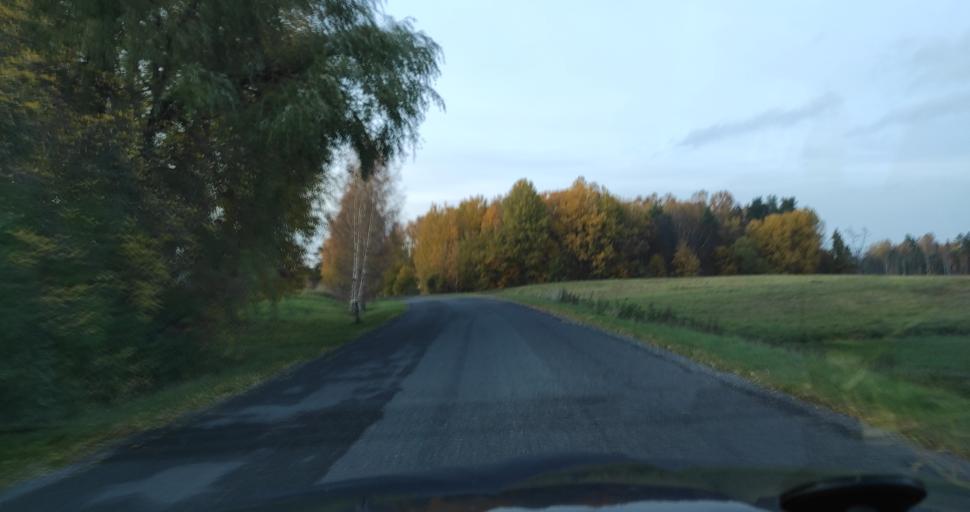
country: LV
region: Aizpute
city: Aizpute
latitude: 56.7079
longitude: 21.7929
